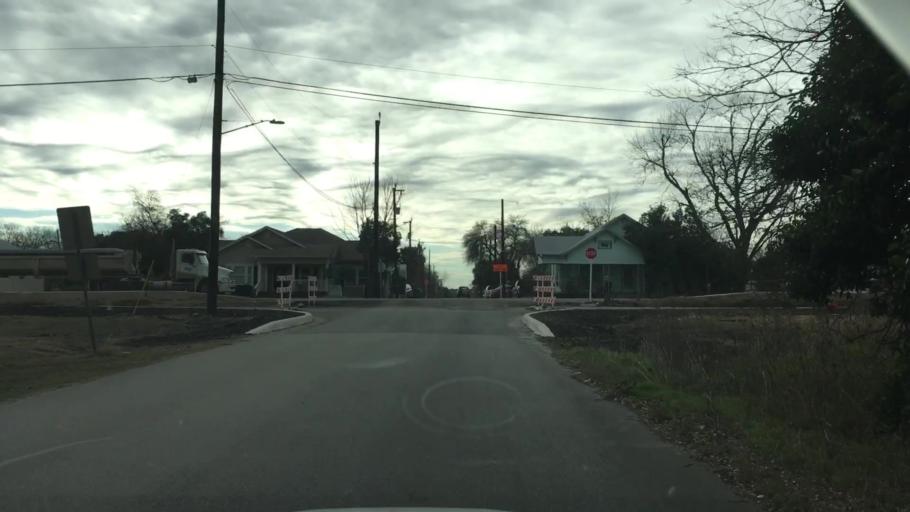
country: US
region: Texas
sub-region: Bexar County
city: Converse
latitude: 29.5164
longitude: -98.3123
